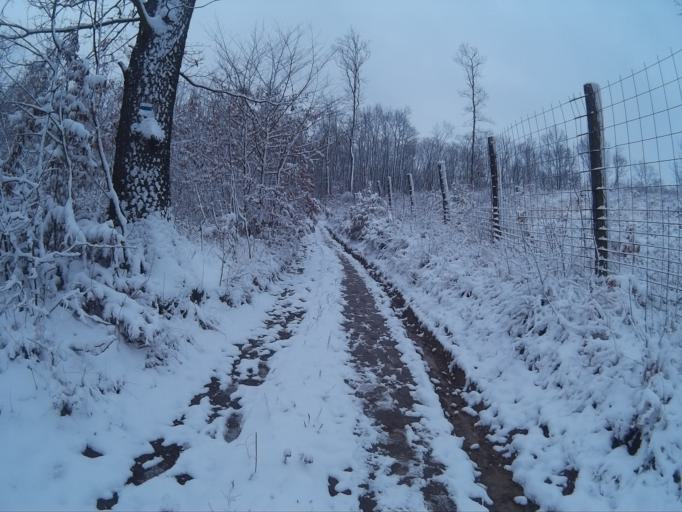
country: HU
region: Fejer
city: Szarliget
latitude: 47.5148
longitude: 18.5097
